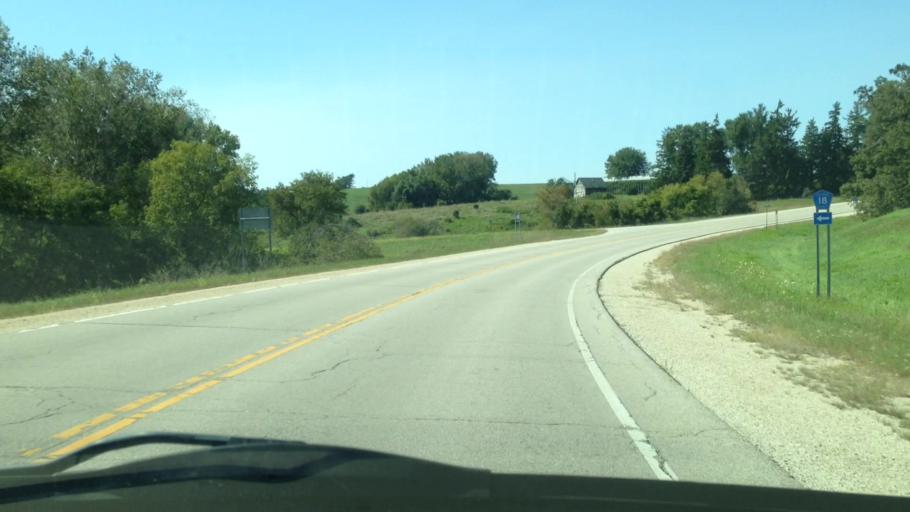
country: US
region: Minnesota
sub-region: Houston County
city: Spring Grove
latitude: 43.6021
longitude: -91.7884
